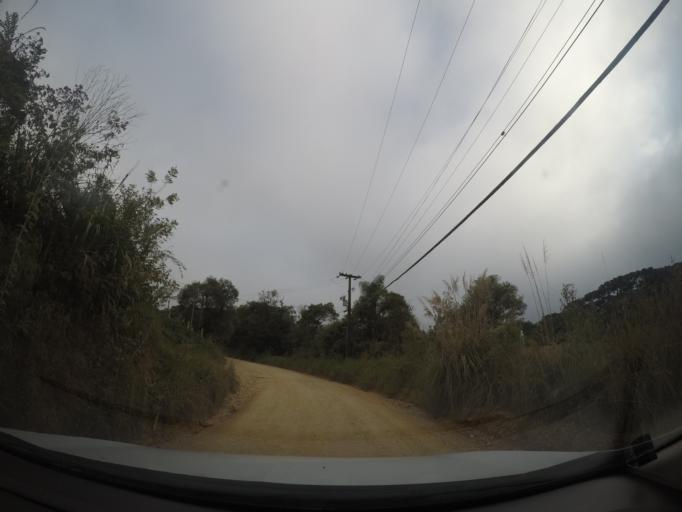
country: BR
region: Parana
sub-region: Colombo
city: Colombo
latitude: -25.3193
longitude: -49.2547
